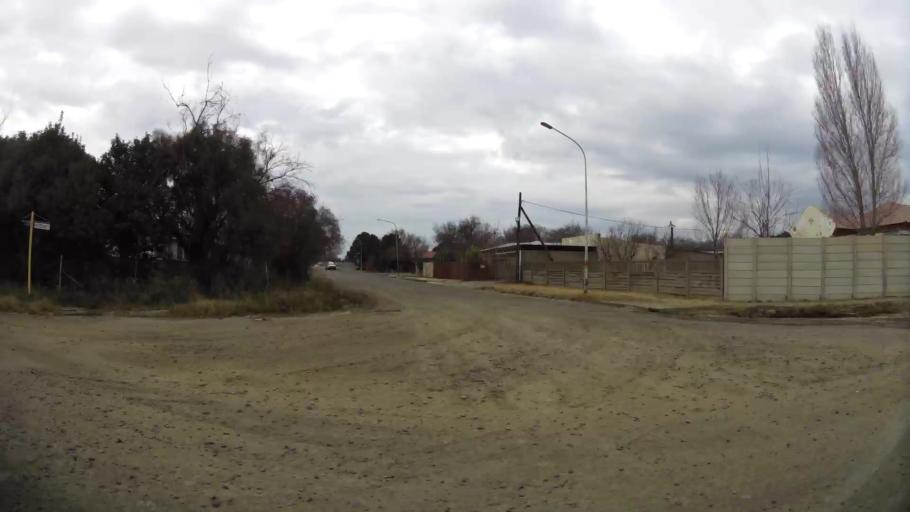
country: ZA
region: Orange Free State
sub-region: Fezile Dabi District Municipality
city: Kroonstad
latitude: -27.6741
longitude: 27.2307
